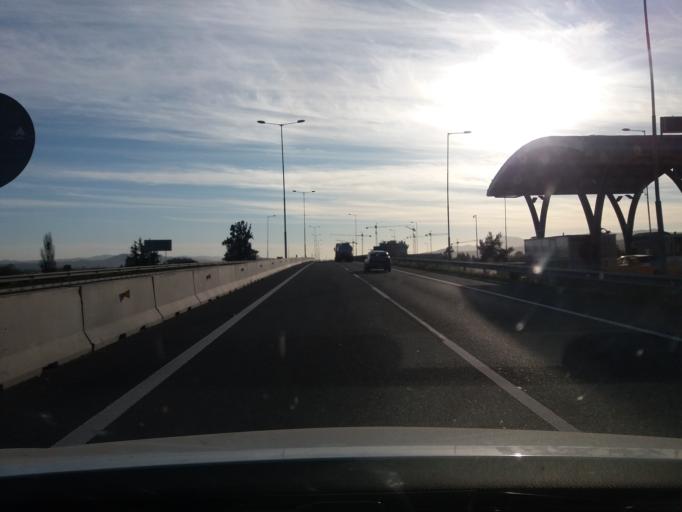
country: CL
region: Valparaiso
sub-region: Provincia de Quillota
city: Quillota
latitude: -32.9015
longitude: -71.2455
